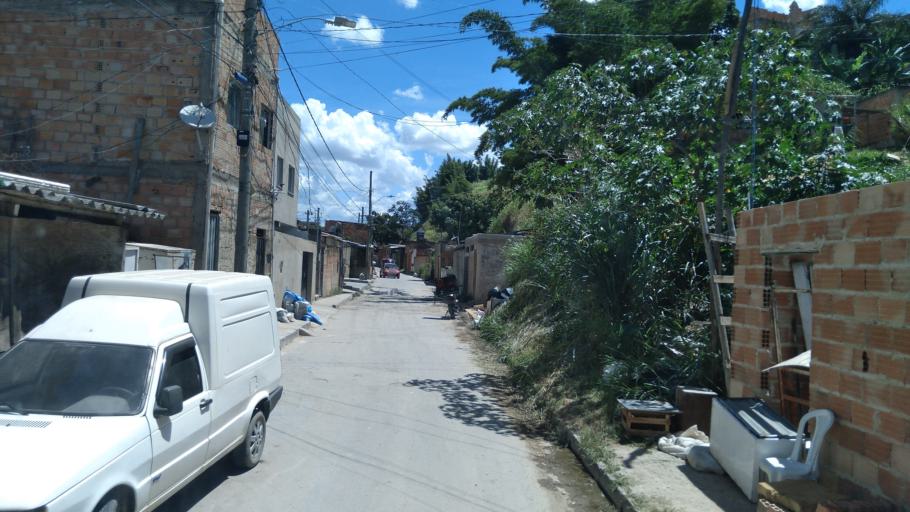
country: BR
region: Minas Gerais
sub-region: Santa Luzia
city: Santa Luzia
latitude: -19.8385
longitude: -43.8968
